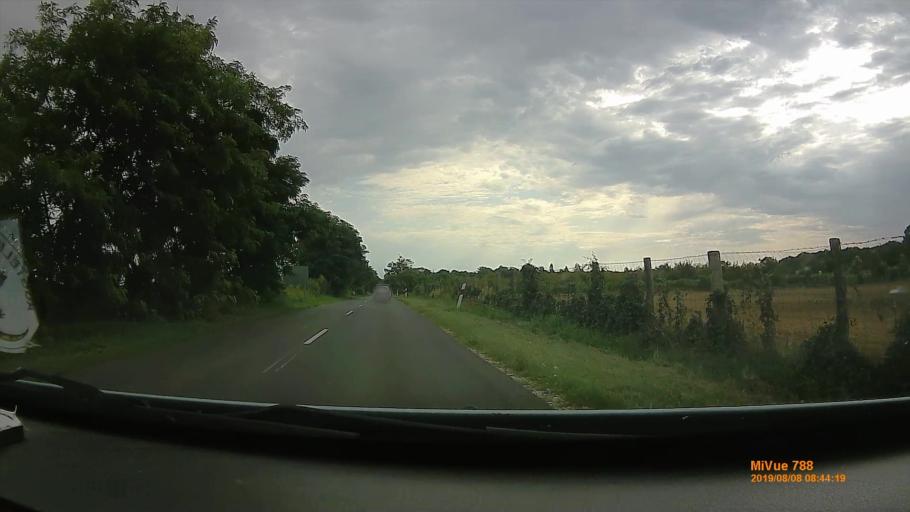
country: HU
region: Hajdu-Bihar
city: Debrecen
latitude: 47.5897
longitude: 21.6331
